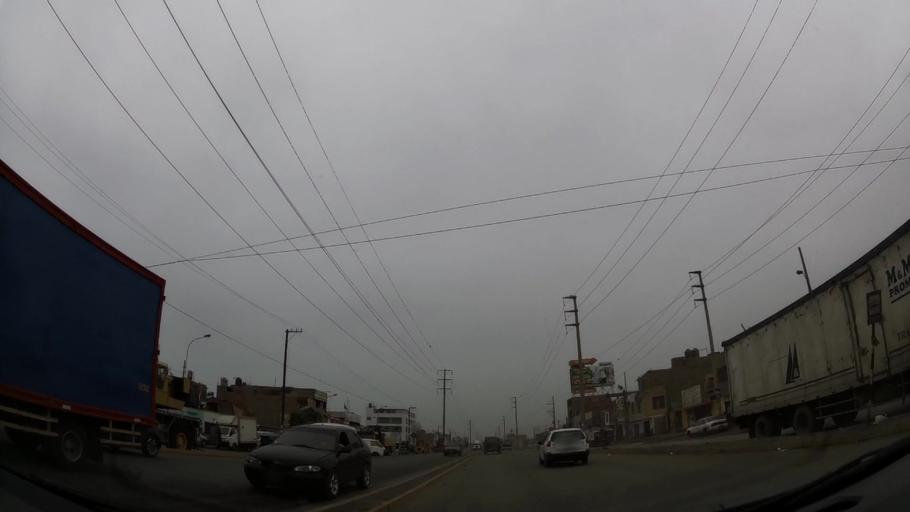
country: PE
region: Lima
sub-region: Lima
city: Punta Hermosa
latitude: -12.2993
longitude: -76.8477
